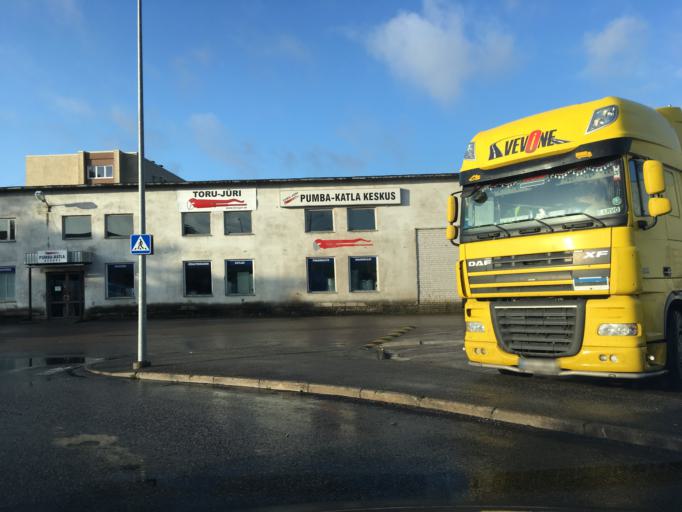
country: EE
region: Harju
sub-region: Tallinna linn
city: Tallinn
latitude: 59.3927
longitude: 24.7180
